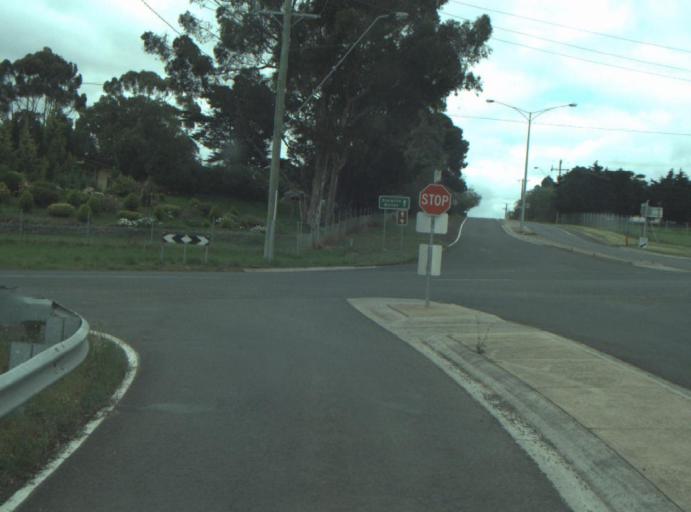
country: AU
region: Victoria
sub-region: Greater Geelong
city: Bell Post Hill
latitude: -38.0708
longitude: 144.3306
